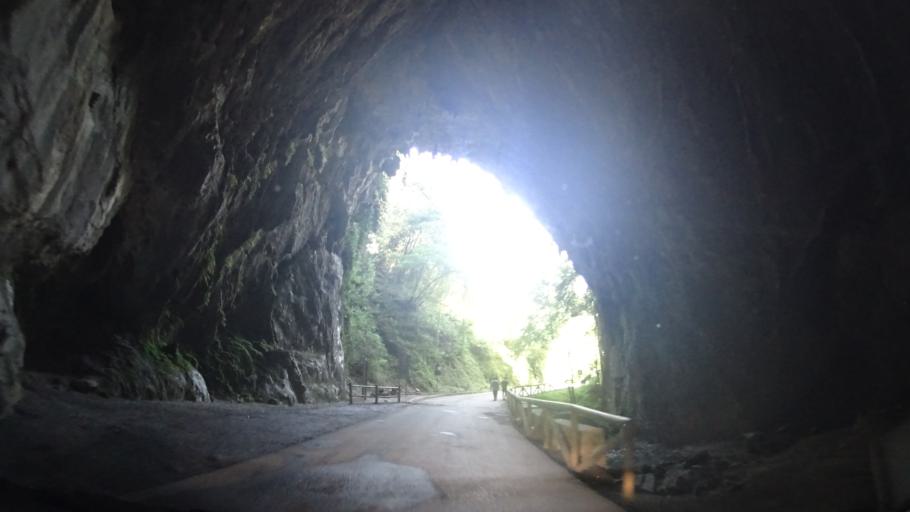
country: ES
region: Asturias
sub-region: Province of Asturias
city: Ribadesella
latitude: 43.4360
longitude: -5.0733
